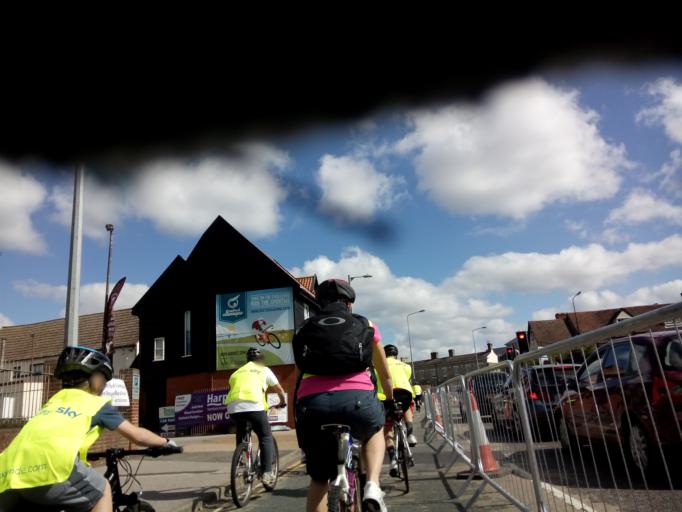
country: GB
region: England
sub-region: Suffolk
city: Ipswich
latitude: 52.0539
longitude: 1.1592
